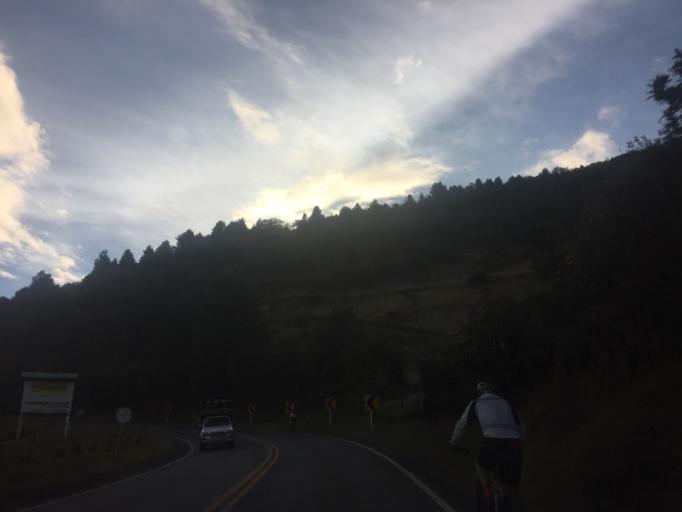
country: CO
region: Narino
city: Pasto
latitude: 1.2579
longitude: -77.2908
